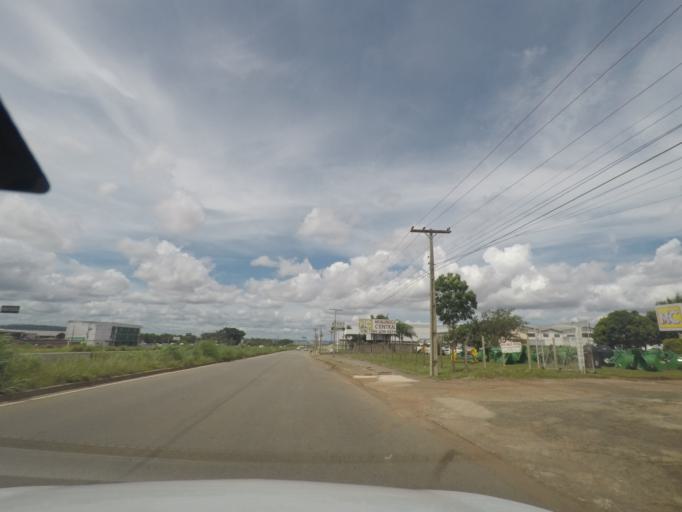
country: BR
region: Goias
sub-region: Goiania
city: Goiania
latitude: -16.7175
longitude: -49.3654
